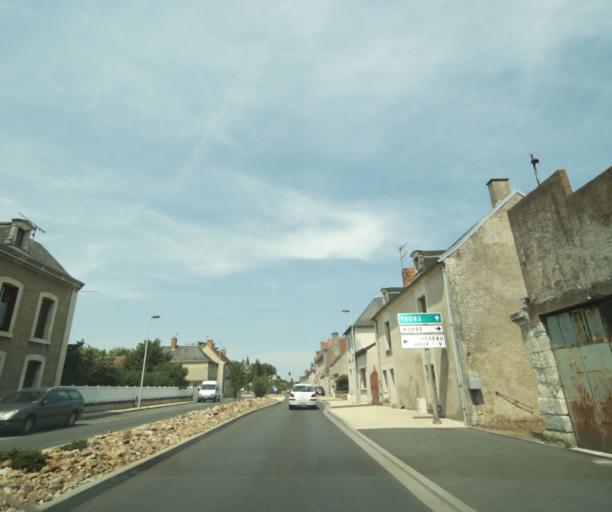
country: FR
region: Poitou-Charentes
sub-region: Departement de la Vienne
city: Antran
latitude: 46.8740
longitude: 0.5637
